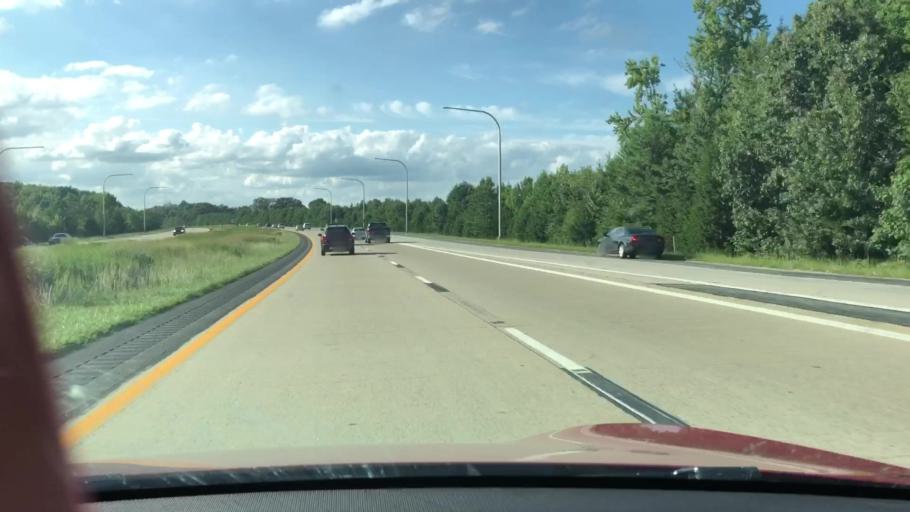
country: US
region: Delaware
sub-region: Kent County
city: Dover
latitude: 39.1707
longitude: -75.4941
